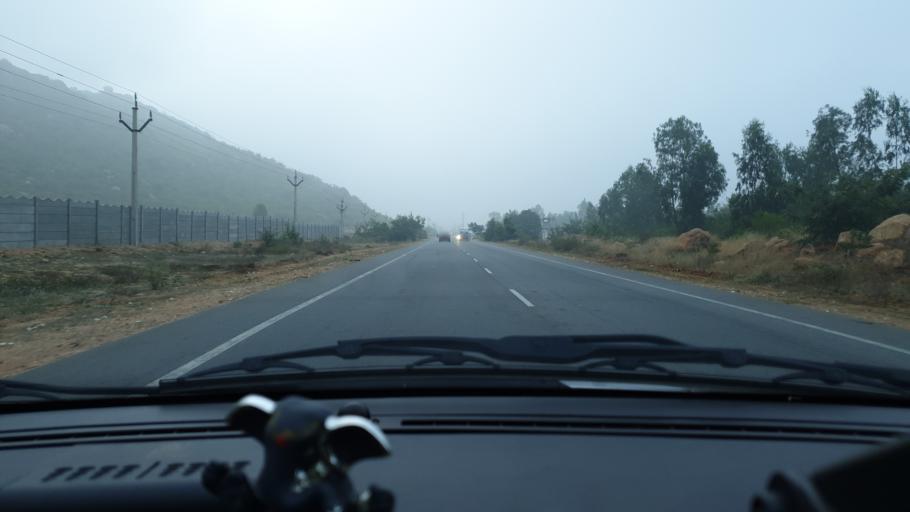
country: IN
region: Telangana
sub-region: Mahbubnagar
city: Farrukhnagar
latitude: 16.9105
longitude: 78.5279
